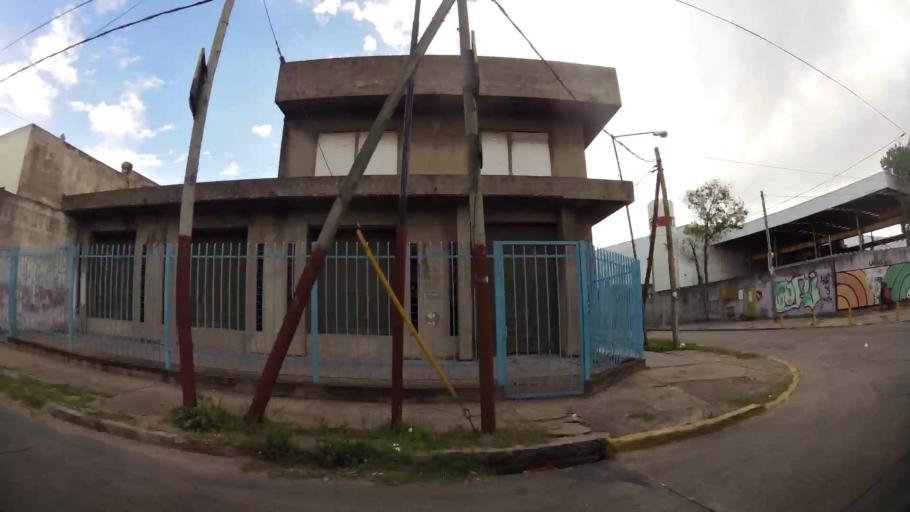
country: AR
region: Buenos Aires
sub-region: Partido de Lanus
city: Lanus
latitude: -34.6990
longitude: -58.3676
